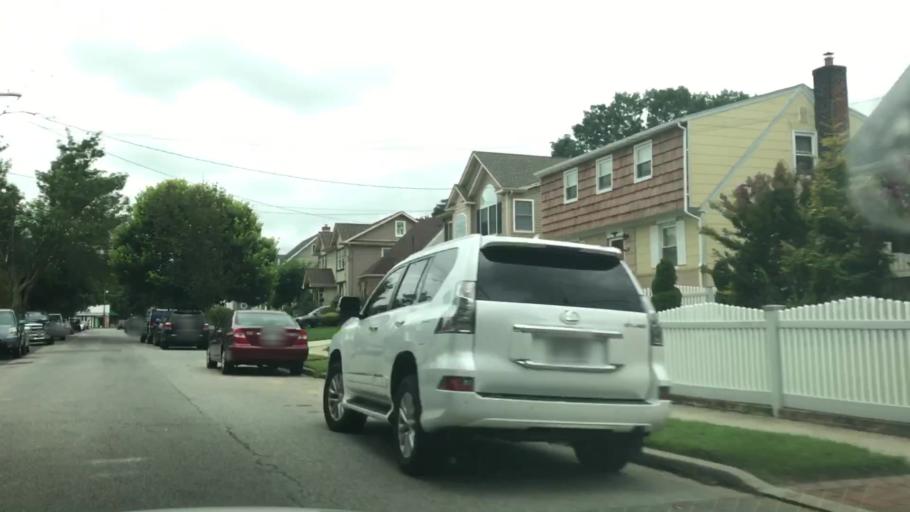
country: US
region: New York
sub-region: Nassau County
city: Hewlett
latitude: 40.6447
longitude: -73.6972
